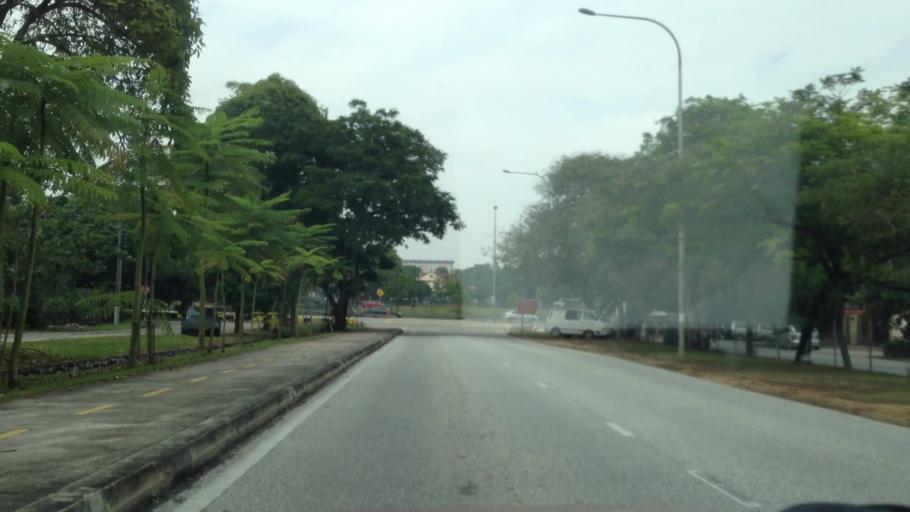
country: MY
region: Selangor
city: Subang Jaya
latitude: 3.0459
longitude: 101.5739
